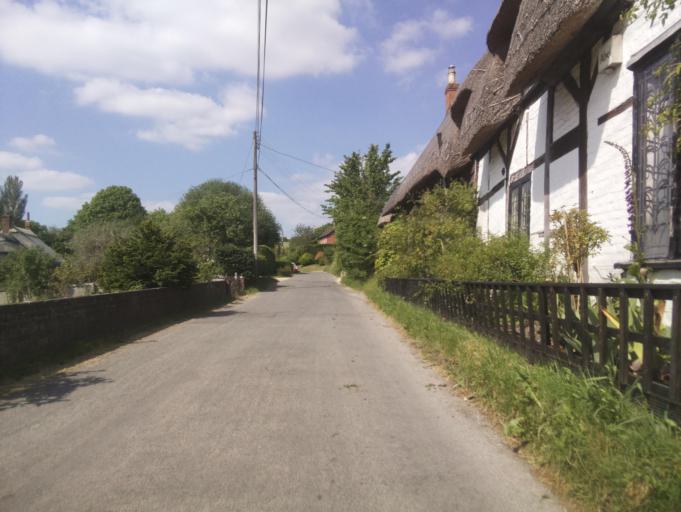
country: GB
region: England
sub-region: Wiltshire
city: Rushall
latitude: 51.2730
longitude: -1.8005
